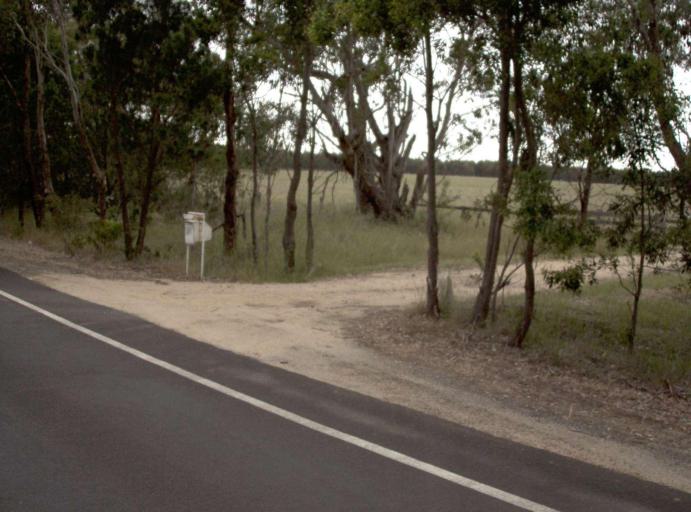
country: AU
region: Victoria
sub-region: Wellington
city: Sale
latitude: -38.4171
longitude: 146.9599
